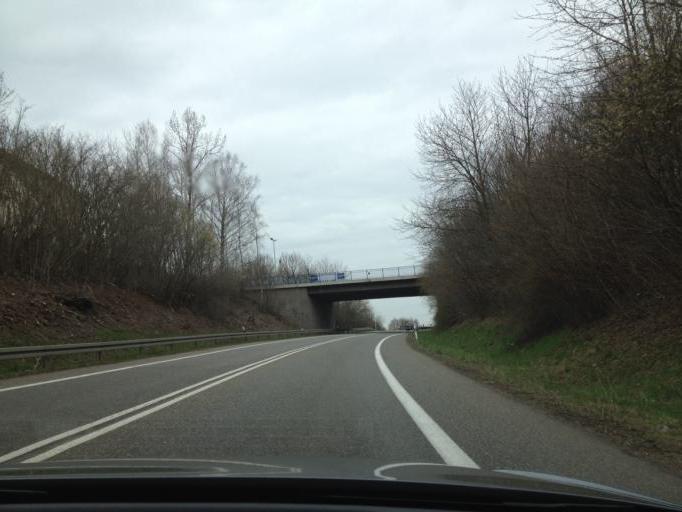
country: DE
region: Saarland
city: Sankt Wendel
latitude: 49.4676
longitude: 7.1491
